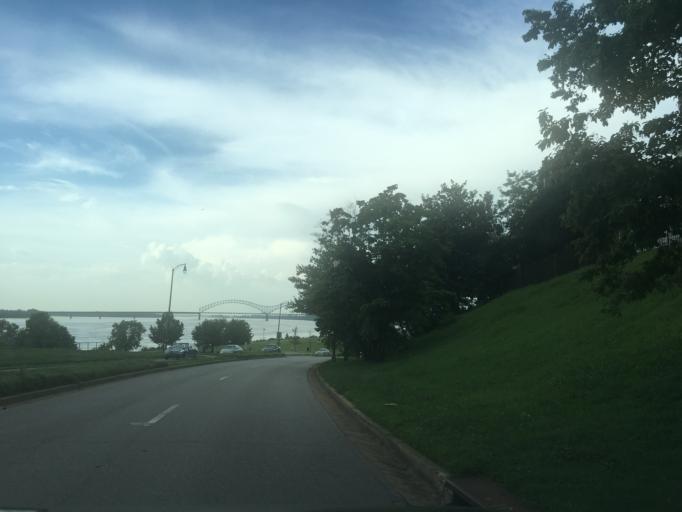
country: US
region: Tennessee
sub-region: Shelby County
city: Memphis
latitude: 35.1312
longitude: -90.0669
